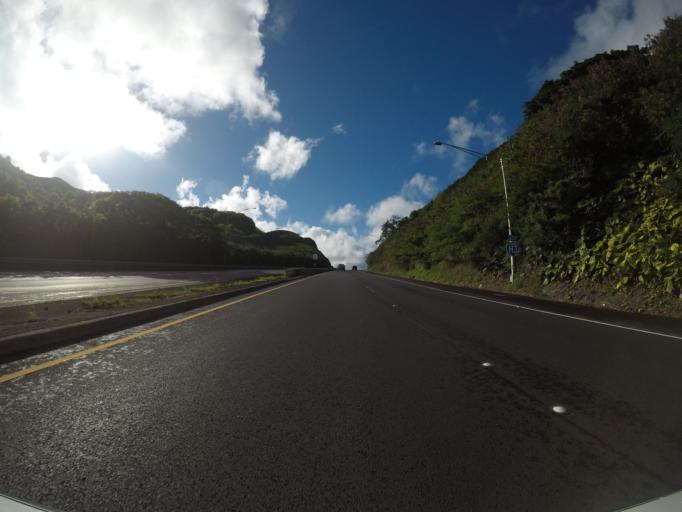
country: US
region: Hawaii
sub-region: Honolulu County
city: Kailua
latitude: 21.4089
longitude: -157.7693
